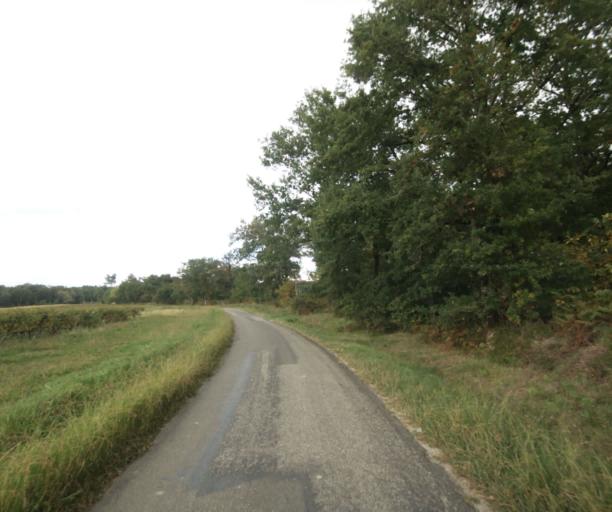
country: FR
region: Midi-Pyrenees
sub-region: Departement du Gers
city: Eauze
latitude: 43.8948
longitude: 0.1106
